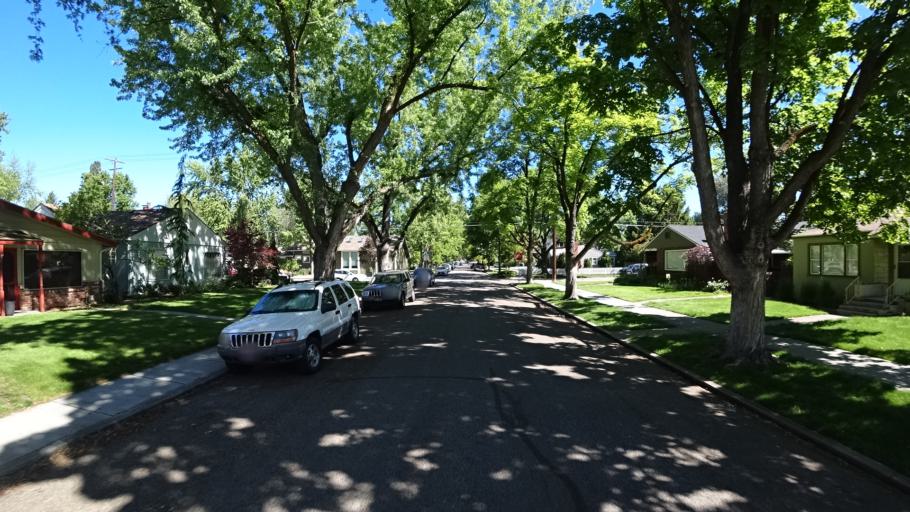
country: US
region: Idaho
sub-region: Ada County
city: Boise
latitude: 43.6317
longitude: -116.2134
